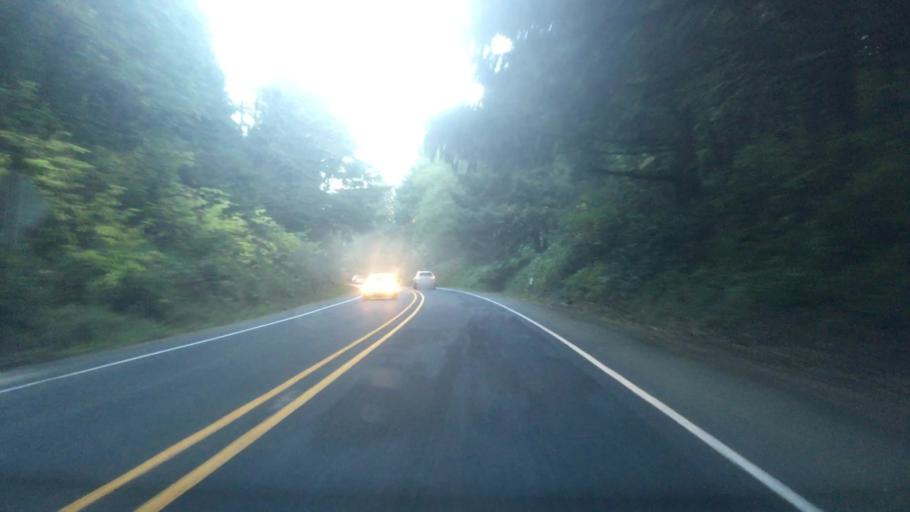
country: US
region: Oregon
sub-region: Clatsop County
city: Cannon Beach
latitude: 45.8837
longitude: -123.9593
